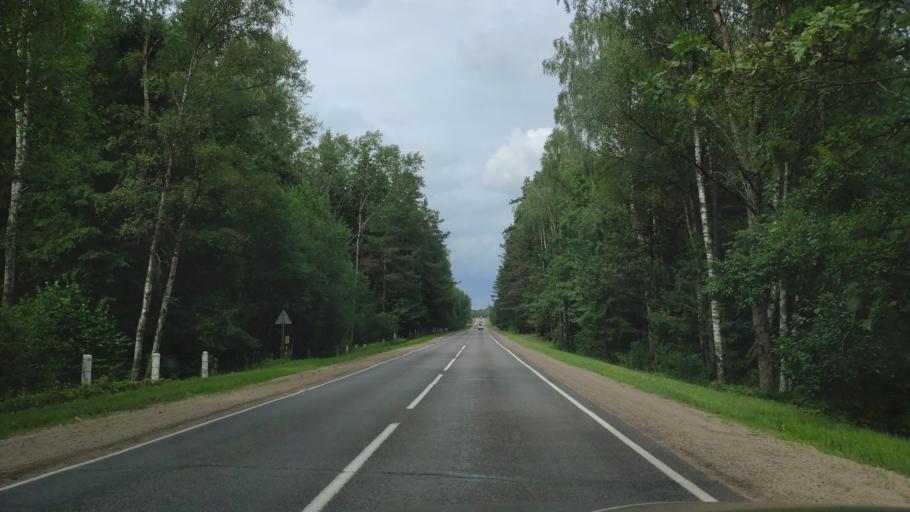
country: BY
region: Minsk
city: Novosel'ye
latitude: 53.9531
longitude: 27.2458
